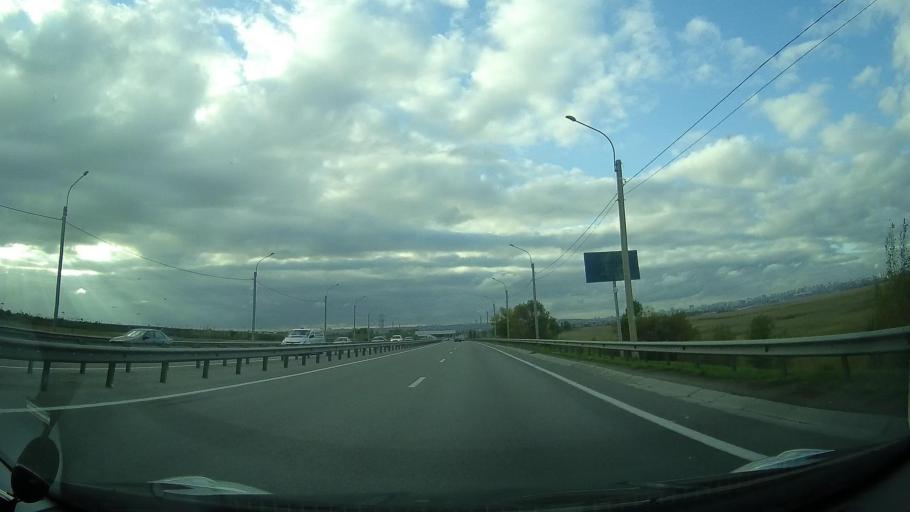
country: RU
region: Rostov
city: Bataysk
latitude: 47.1664
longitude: 39.7548
